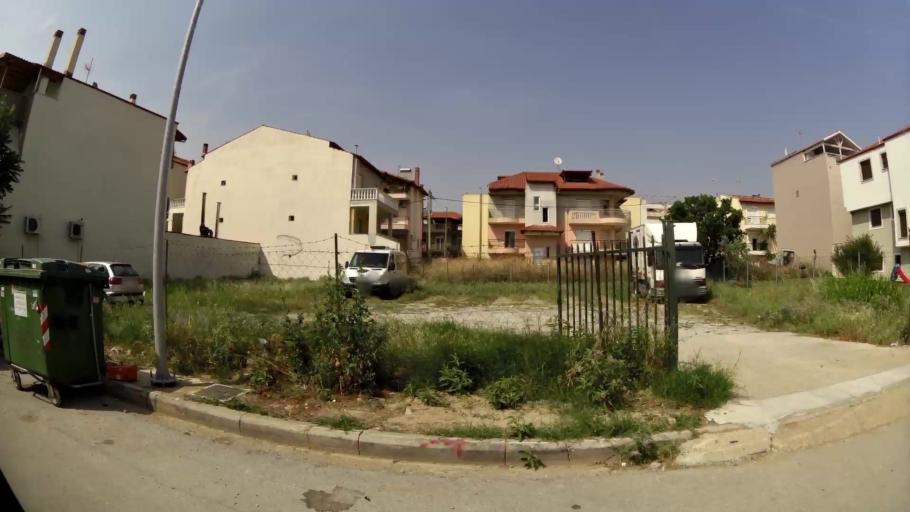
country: GR
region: Central Macedonia
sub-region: Nomos Thessalonikis
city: Efkarpia
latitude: 40.6844
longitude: 22.9468
